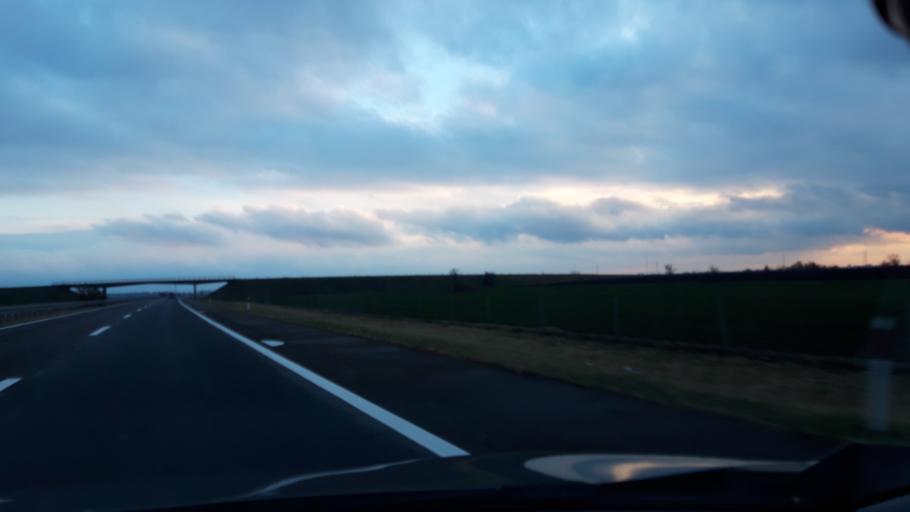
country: RS
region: Autonomna Pokrajina Vojvodina
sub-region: Juznobacki Okrug
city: Vrbas
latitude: 45.5786
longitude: 19.7196
